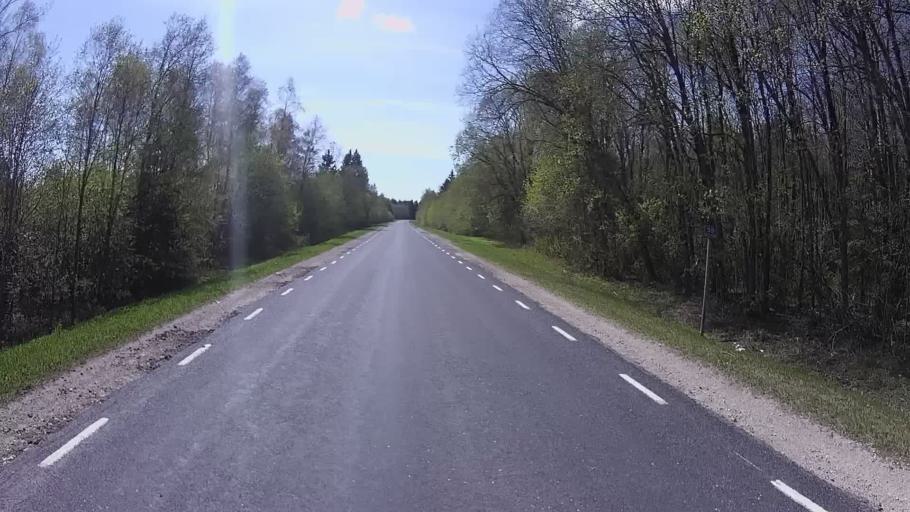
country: EE
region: Laeaene
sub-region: Ridala Parish
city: Uuemoisa
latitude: 59.0110
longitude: 23.7838
